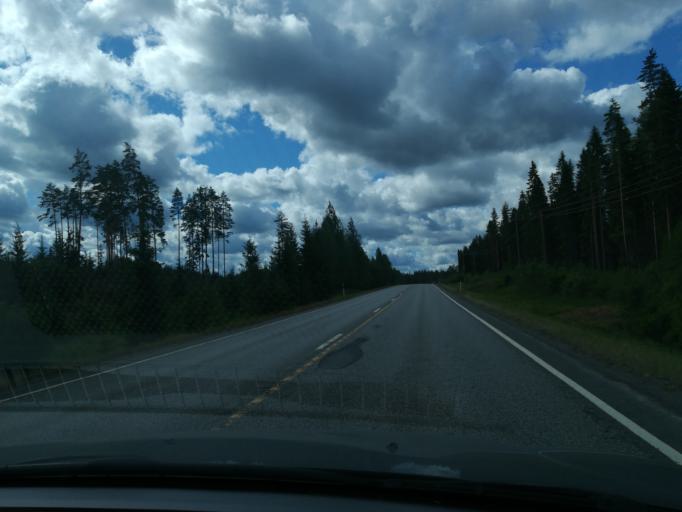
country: FI
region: Southern Savonia
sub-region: Mikkeli
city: Ristiina
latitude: 61.4685
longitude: 27.2547
